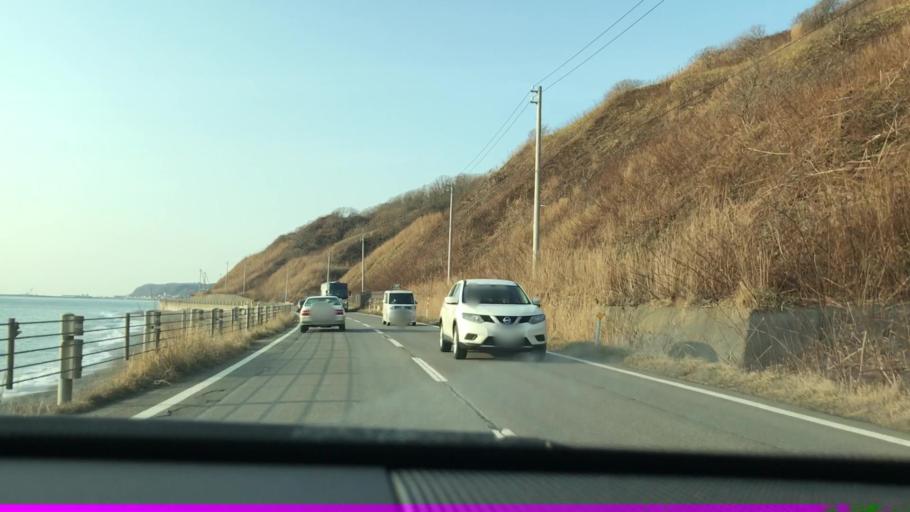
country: JP
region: Hokkaido
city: Shizunai-furukawacho
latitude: 42.2358
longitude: 142.5990
